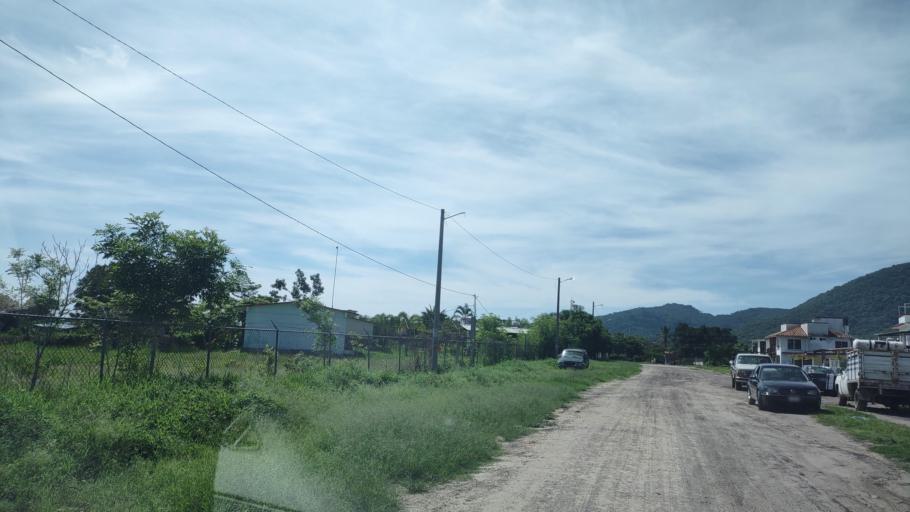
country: MX
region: Veracruz
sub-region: Emiliano Zapata
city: Dos Rios
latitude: 19.4284
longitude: -96.7985
